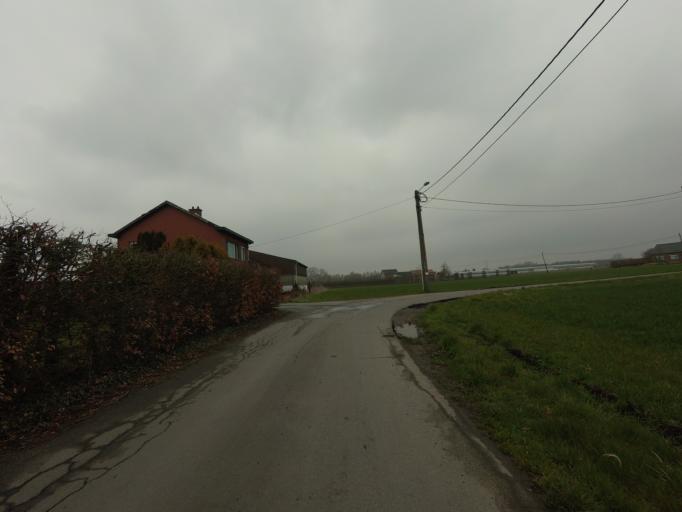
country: BE
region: Flanders
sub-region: Provincie Antwerpen
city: Putte
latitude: 51.0752
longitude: 4.5913
